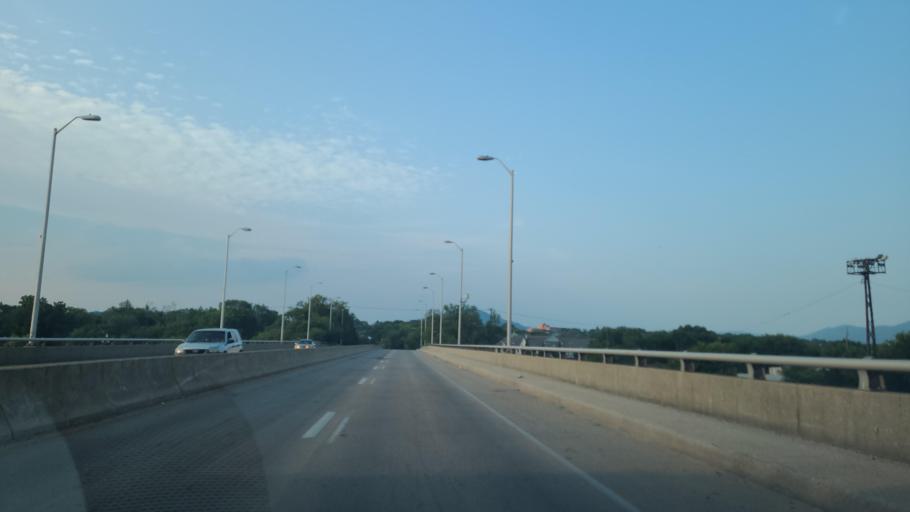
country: US
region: Virginia
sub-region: City of Roanoke
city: Roanoke
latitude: 37.2754
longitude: -79.9576
